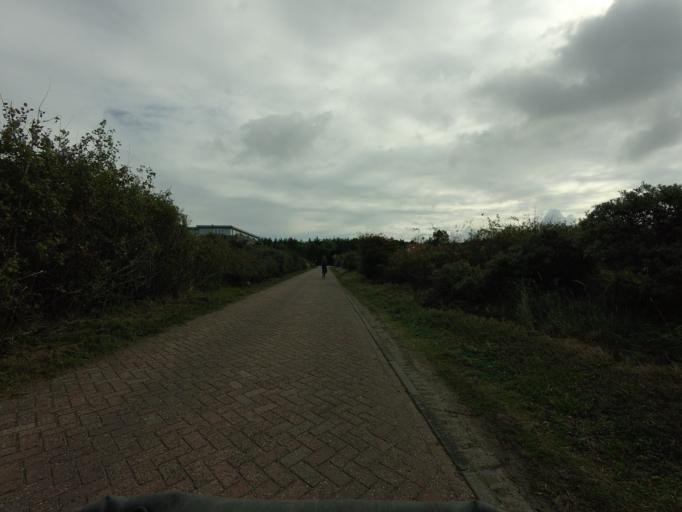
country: NL
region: Friesland
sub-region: Gemeente Ameland
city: Nes
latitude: 53.4564
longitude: 5.7757
